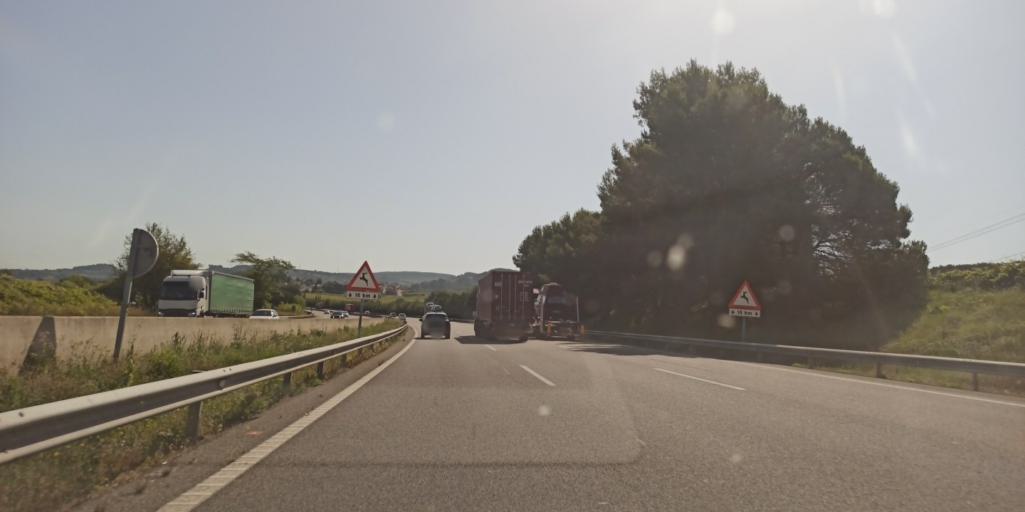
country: ES
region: Catalonia
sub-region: Provincia de Barcelona
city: La Granada
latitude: 41.3865
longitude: 1.7529
